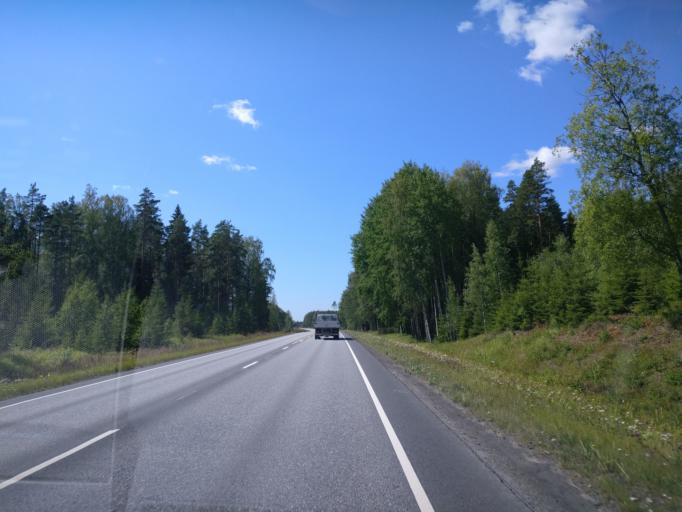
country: FI
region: Satakunta
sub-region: Pori
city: Kullaa
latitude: 61.4612
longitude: 22.1114
